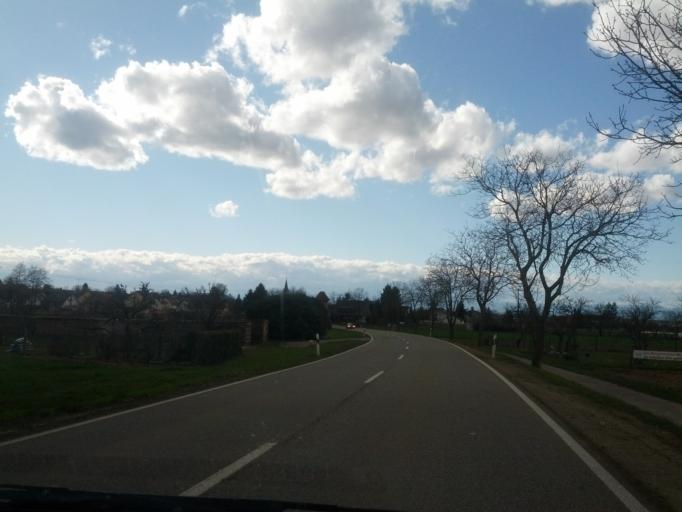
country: DE
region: Baden-Wuerttemberg
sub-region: Freiburg Region
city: Eschbach
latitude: 47.8891
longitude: 7.6658
